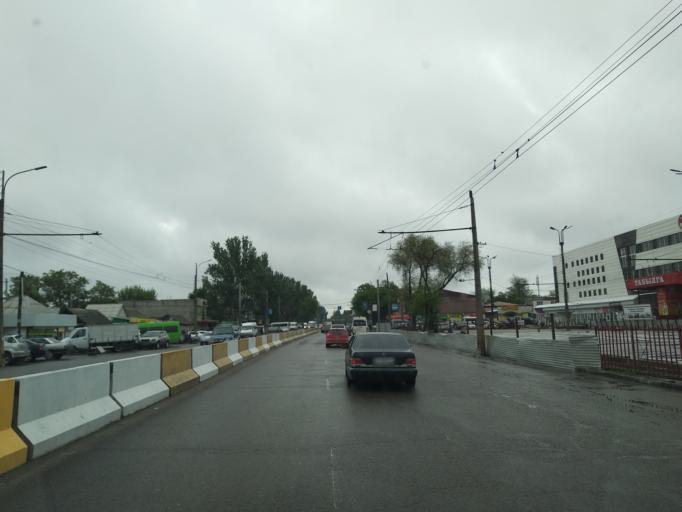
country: KG
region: Chuy
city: Lebedinovka
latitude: 42.8883
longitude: 74.6378
